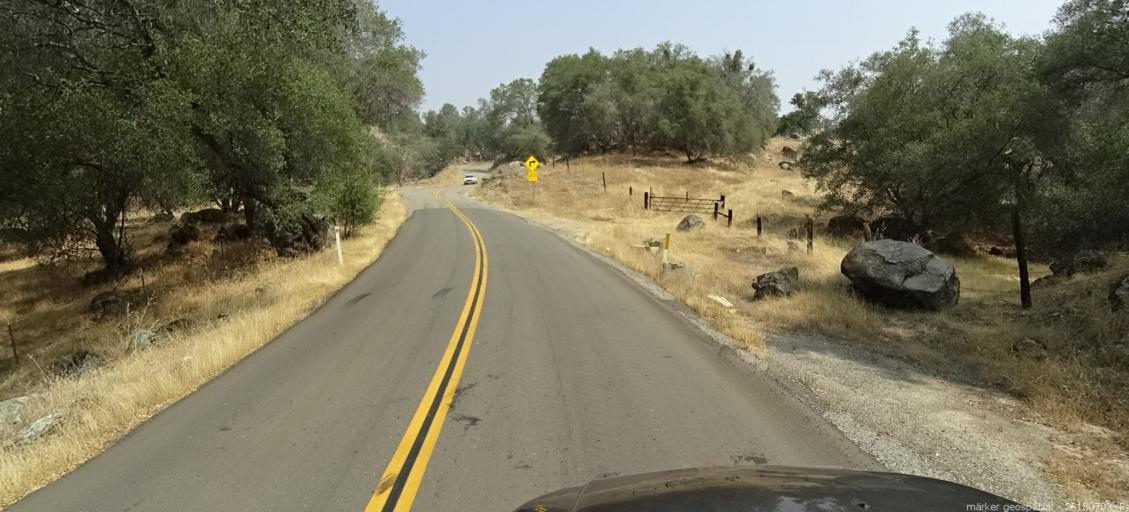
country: US
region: California
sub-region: Madera County
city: Yosemite Lakes
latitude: 37.0836
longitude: -119.6985
